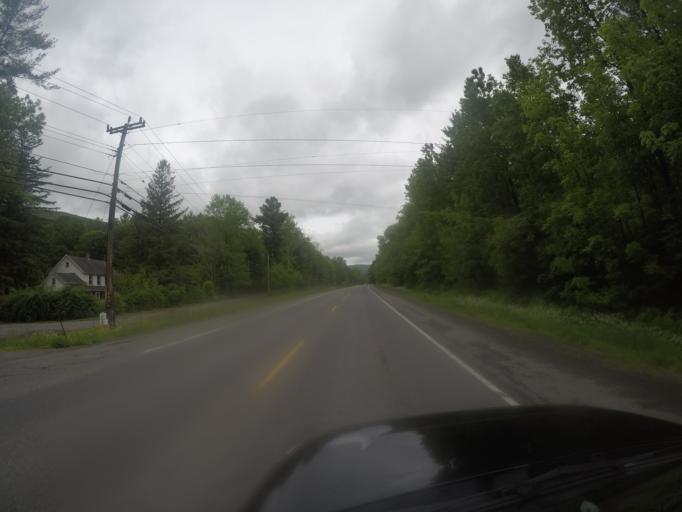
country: US
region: New York
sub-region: Ulster County
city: Shokan
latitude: 42.0953
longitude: -74.3377
